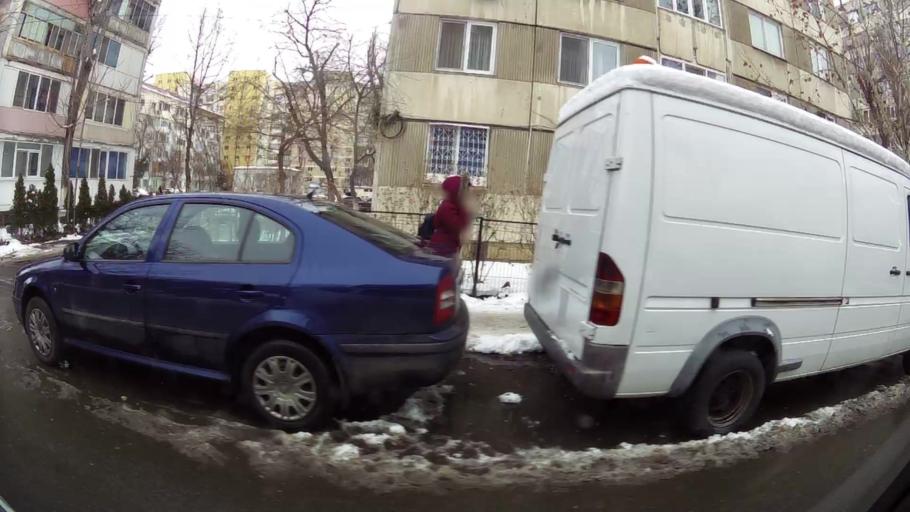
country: RO
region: Ilfov
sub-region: Comuna Popesti-Leordeni
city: Popesti-Leordeni
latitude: 44.3891
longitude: 26.1288
